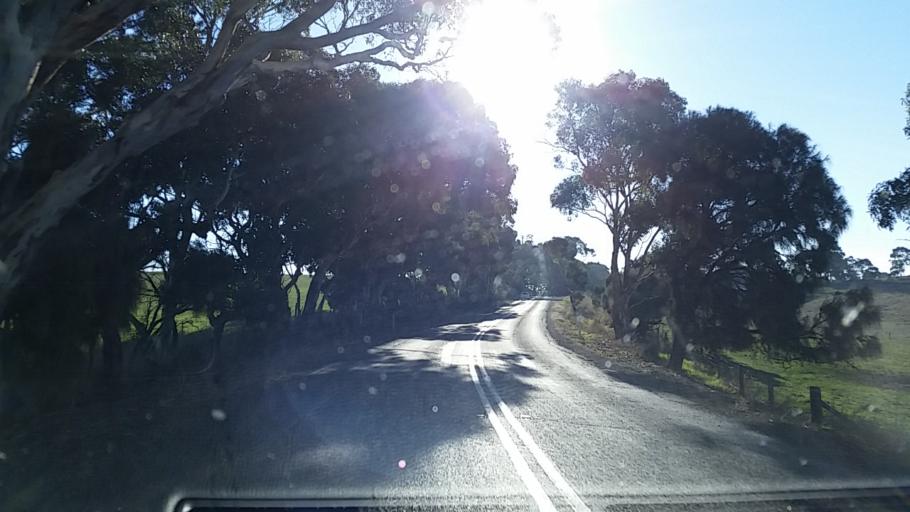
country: AU
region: South Australia
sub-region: Mount Barker
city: Mount Barker
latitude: -35.1257
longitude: 138.9035
